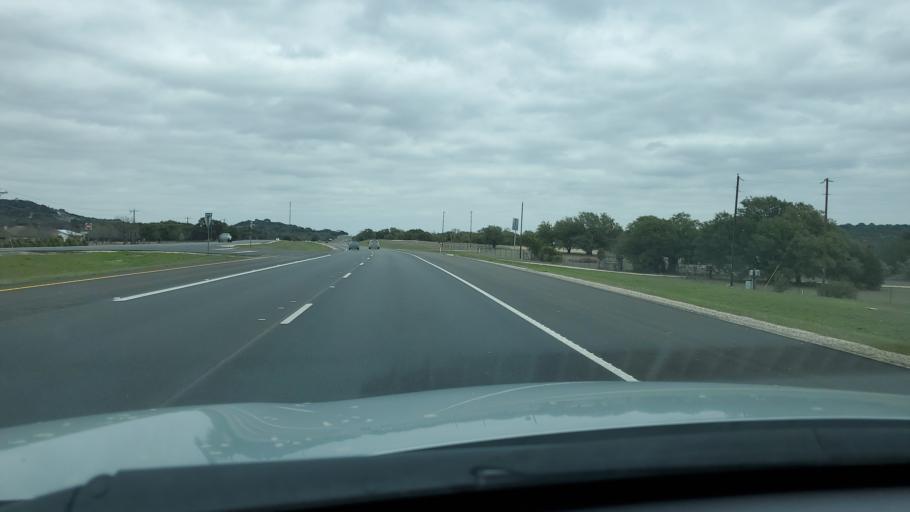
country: US
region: Texas
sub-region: Bell County
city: Killeen
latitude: 30.9925
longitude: -97.7637
